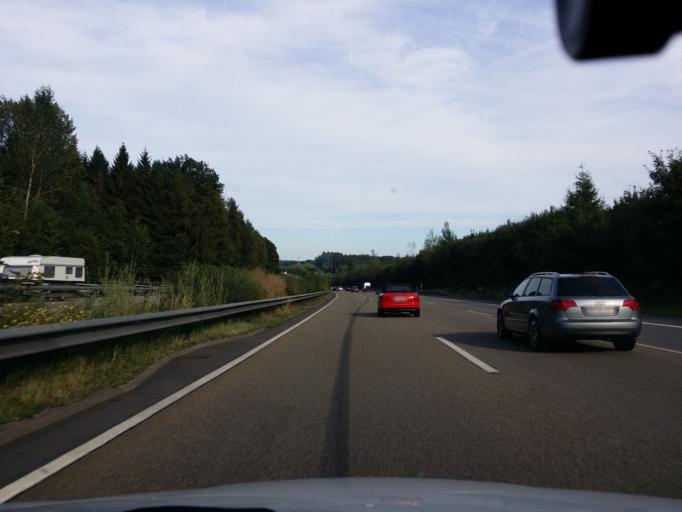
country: DE
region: Rheinland-Pfalz
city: Kleinmaischeid
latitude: 50.5238
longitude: 7.6228
